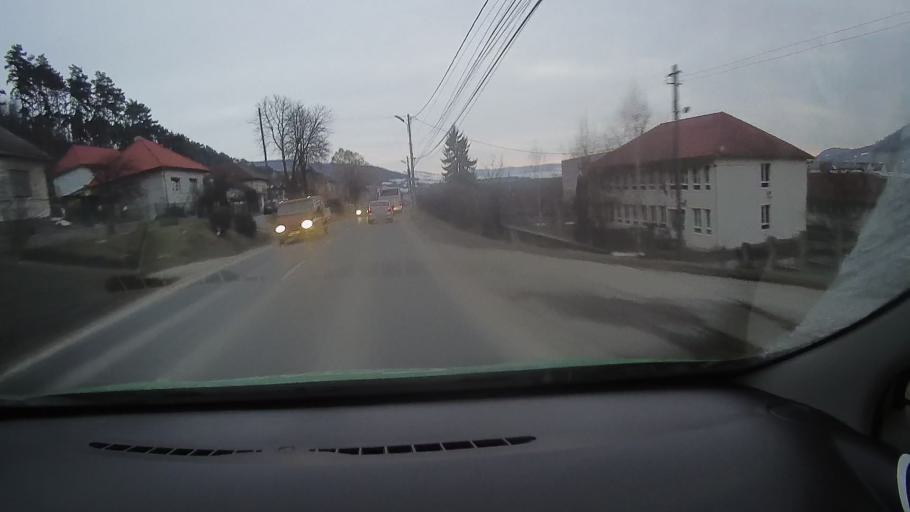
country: RO
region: Harghita
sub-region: Municipiul Odorheiu Secuiesc
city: Odorheiu Secuiesc
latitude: 46.2932
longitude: 25.2898
